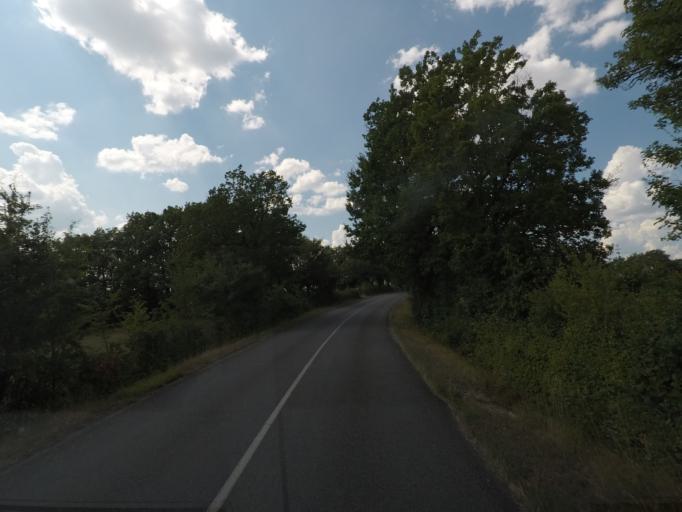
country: FR
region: Midi-Pyrenees
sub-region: Departement du Lot
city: Le Vigan
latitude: 44.6380
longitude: 1.5879
